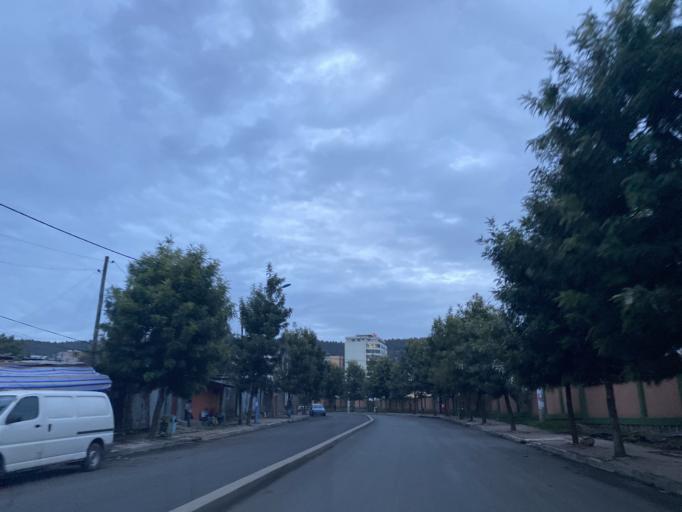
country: ET
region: Adis Abeba
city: Addis Ababa
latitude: 9.0167
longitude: 38.8116
